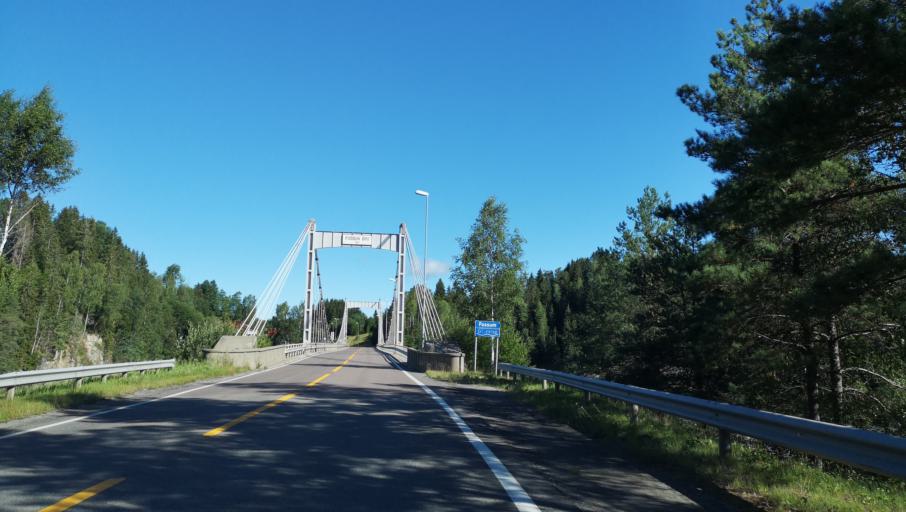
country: NO
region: Ostfold
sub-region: Spydeberg
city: Spydeberg
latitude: 59.6021
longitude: 11.1028
